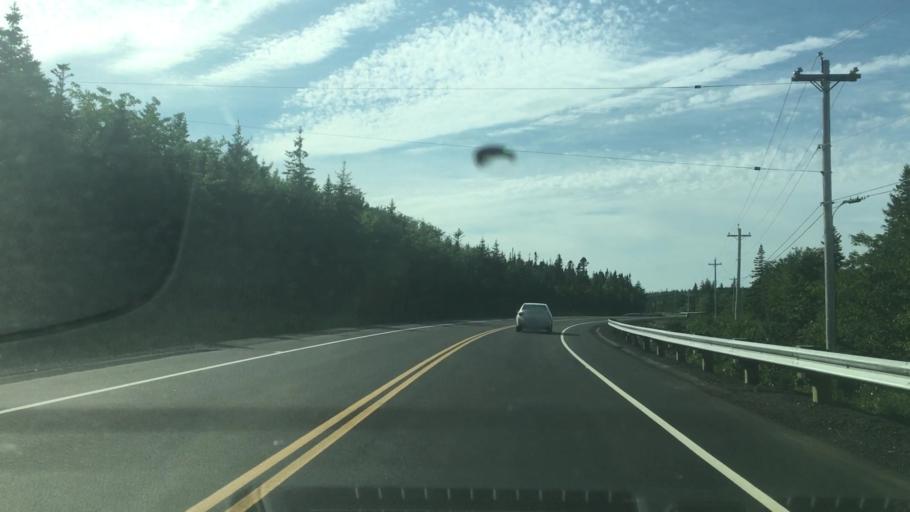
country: CA
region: Nova Scotia
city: Sydney Mines
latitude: 46.8404
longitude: -60.3902
